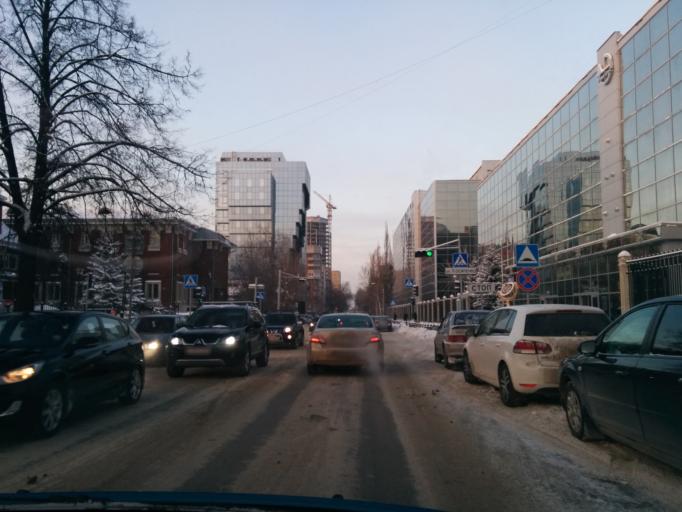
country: RU
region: Perm
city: Perm
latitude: 57.9993
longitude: 56.2635
